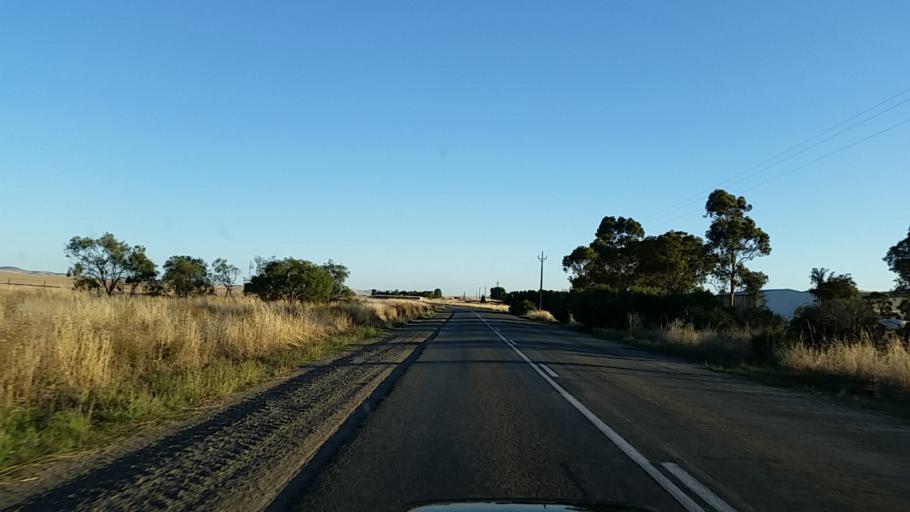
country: AU
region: South Australia
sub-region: Northern Areas
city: Jamestown
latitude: -33.4697
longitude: 138.5930
